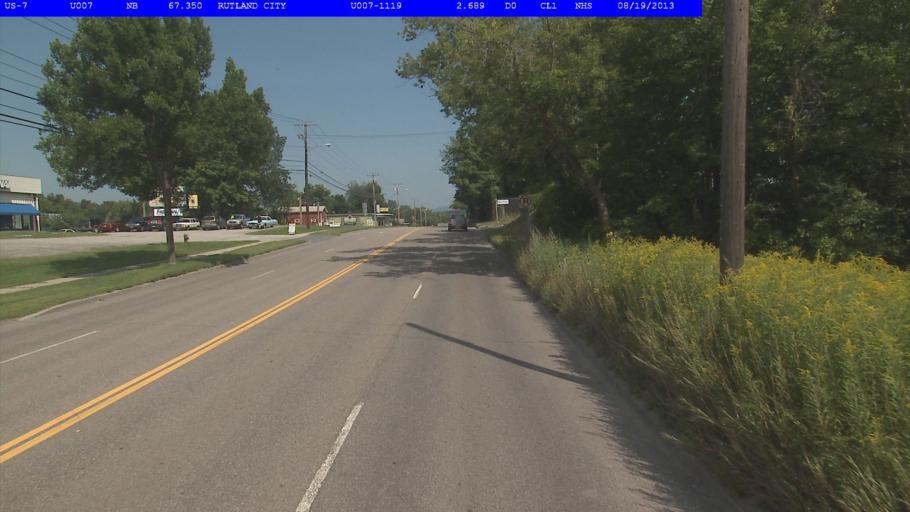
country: US
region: Vermont
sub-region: Rutland County
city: Rutland
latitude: 43.6283
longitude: -72.9758
